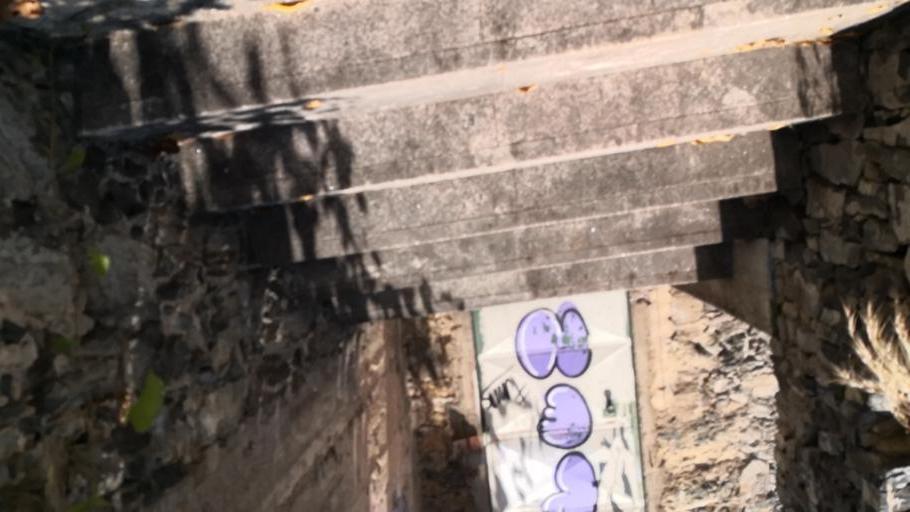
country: PT
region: Braganca
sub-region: Braganca Municipality
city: Braganca
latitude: 41.8041
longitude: -6.7553
